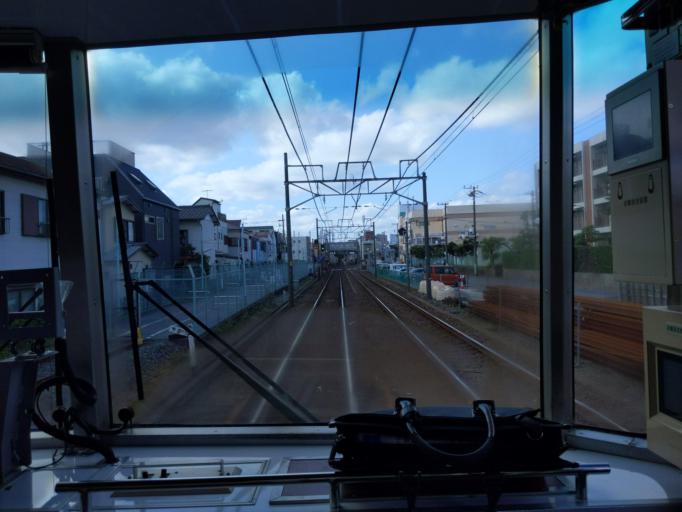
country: JP
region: Chiba
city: Funabashi
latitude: 35.7288
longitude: 140.0316
